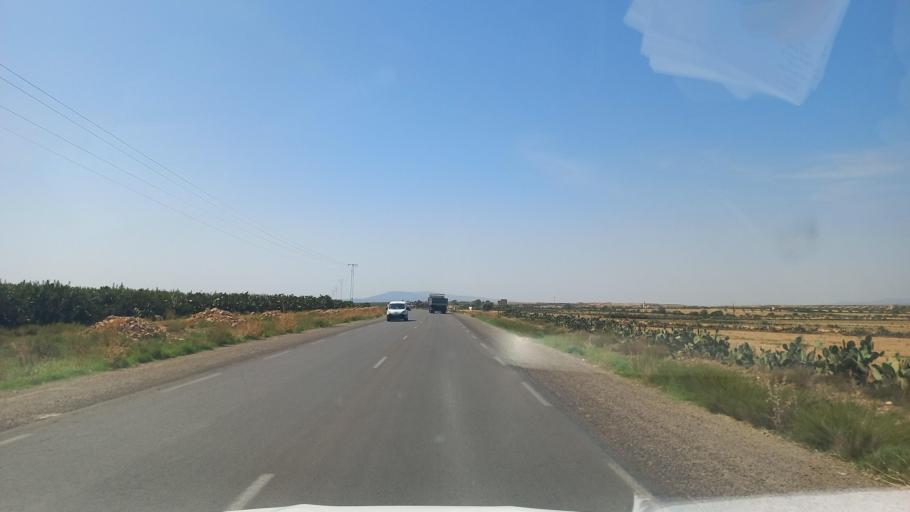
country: TN
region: Al Qasrayn
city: Sbiba
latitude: 35.3704
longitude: 9.0980
